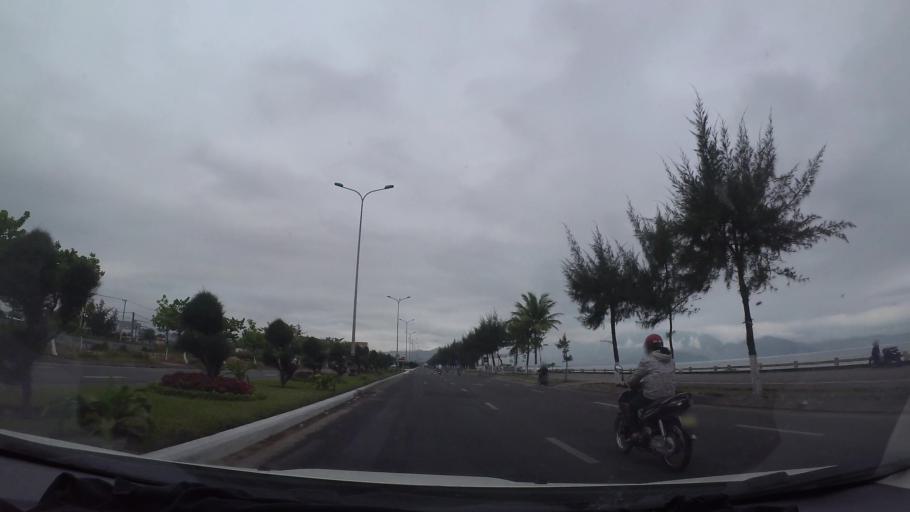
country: VN
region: Da Nang
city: Lien Chieu
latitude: 16.0867
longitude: 108.1575
